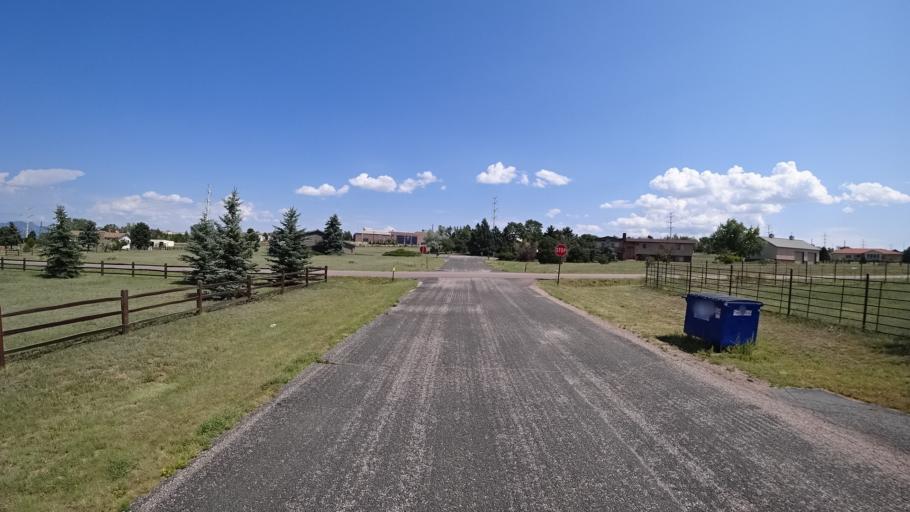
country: US
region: Colorado
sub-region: El Paso County
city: Air Force Academy
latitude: 38.9386
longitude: -104.7784
